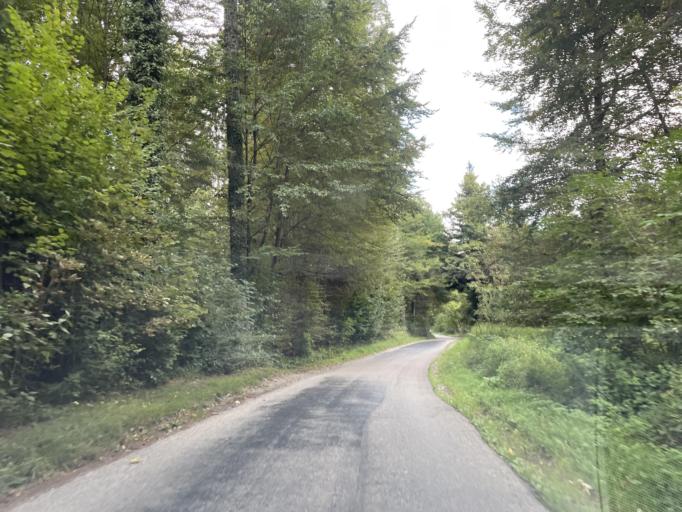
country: CH
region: Zurich
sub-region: Bezirk Winterthur
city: Seen (Kreis 3) / Ganzenbuehl
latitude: 47.4735
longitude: 8.7611
